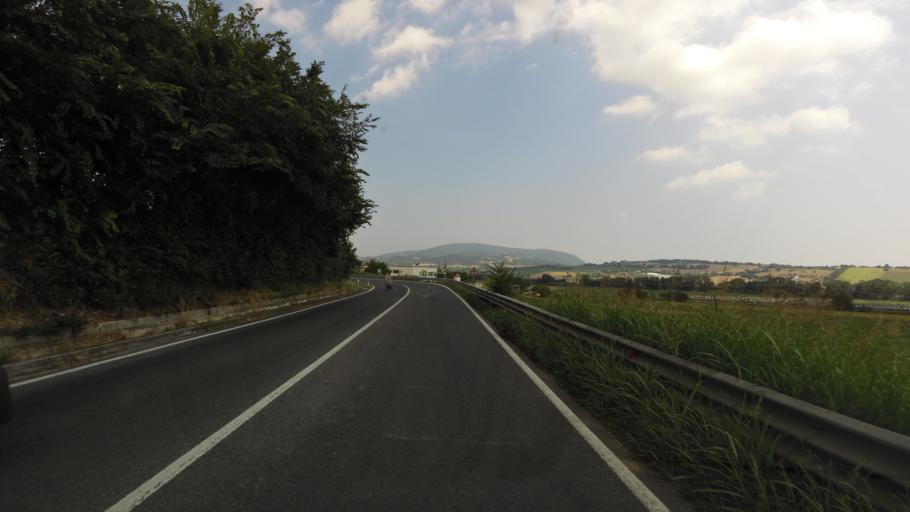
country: IT
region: The Marches
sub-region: Provincia di Ancona
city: Castelfidardo
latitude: 43.4825
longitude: 13.5783
